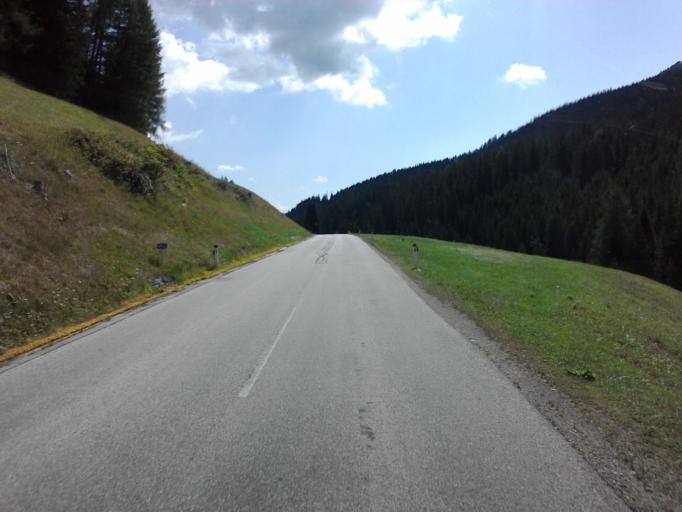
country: AT
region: Tyrol
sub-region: Politischer Bezirk Lienz
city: Kartitsch
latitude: 46.7194
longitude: 12.5295
